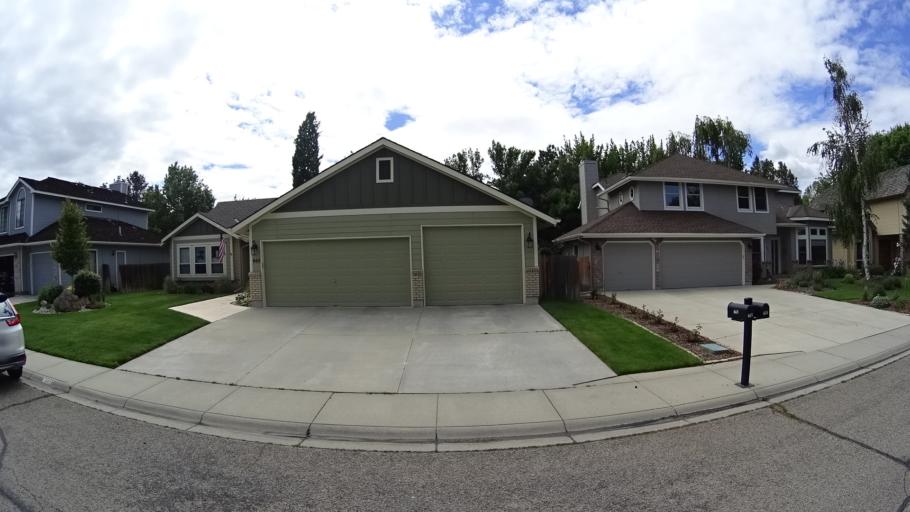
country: US
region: Idaho
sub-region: Ada County
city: Boise
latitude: 43.5715
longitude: -116.1751
